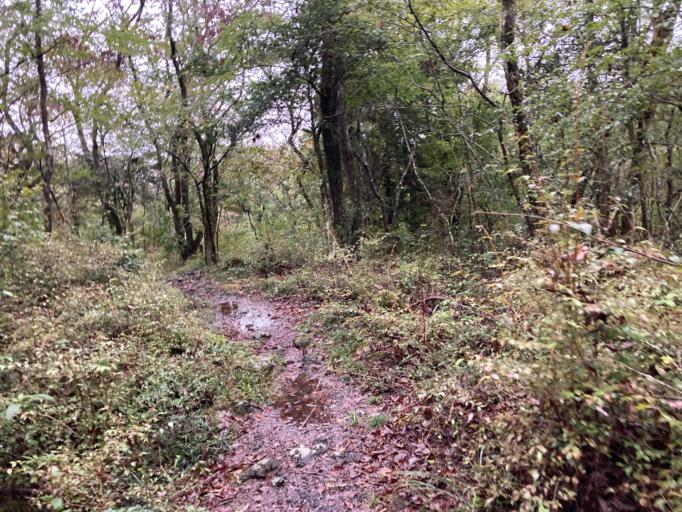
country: JP
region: Shizuoka
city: Fuji
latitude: 35.2428
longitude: 138.7284
